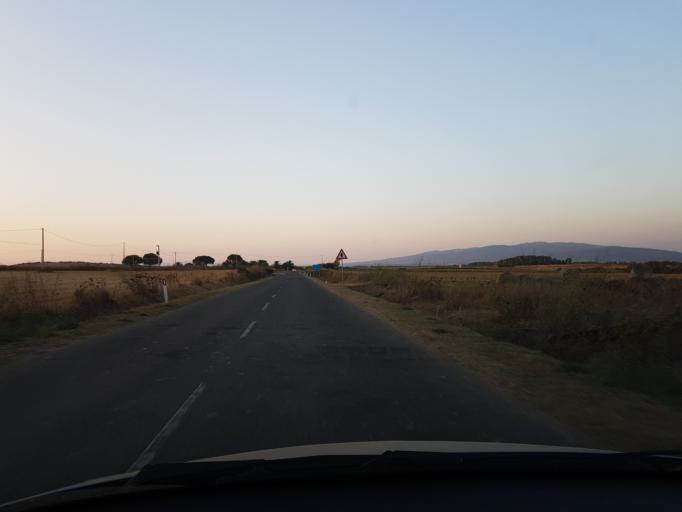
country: IT
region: Sardinia
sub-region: Provincia di Oristano
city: Nurachi
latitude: 39.9821
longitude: 8.4545
